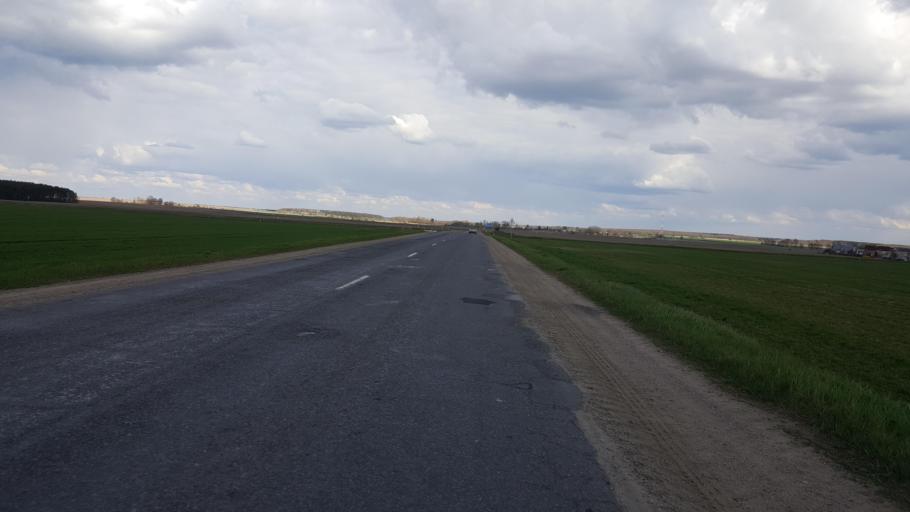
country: BY
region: Brest
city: Kamyanyets
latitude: 52.4151
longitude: 23.6330
